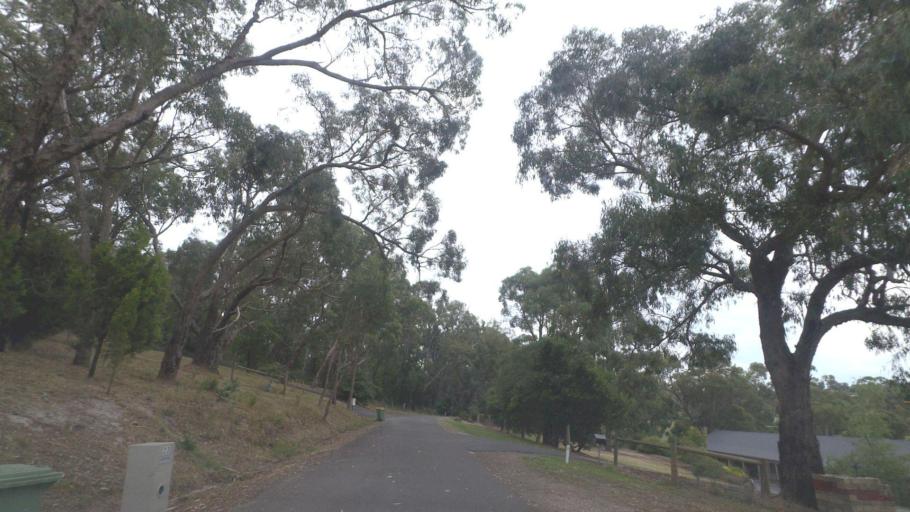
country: AU
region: Victoria
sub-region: Yarra Ranges
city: Mount Evelyn
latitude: -37.7574
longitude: 145.3803
